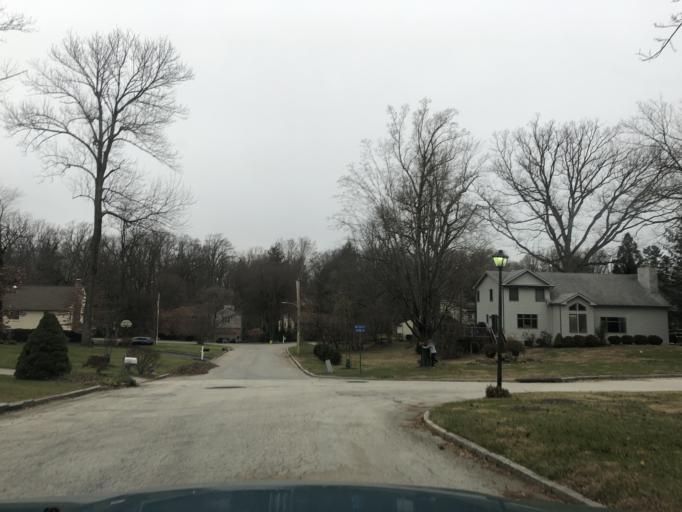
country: US
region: Pennsylvania
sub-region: Delaware County
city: Radnor
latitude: 40.0306
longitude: -75.3547
